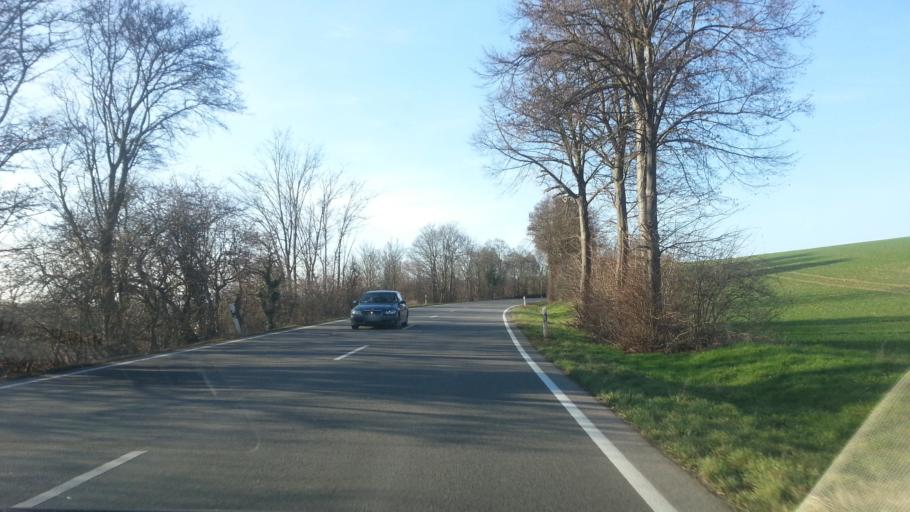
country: DE
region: Rheinland-Pfalz
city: Immesheim
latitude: 49.6486
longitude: 8.1101
